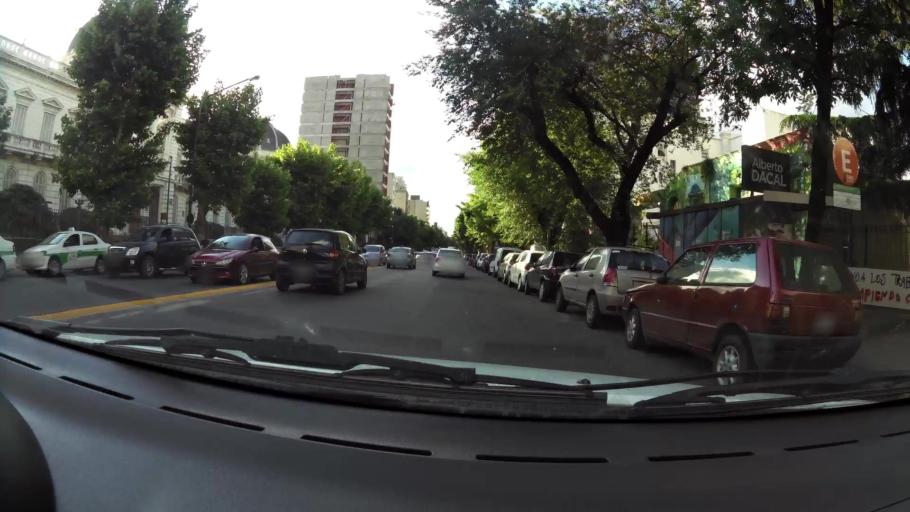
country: AR
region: Buenos Aires
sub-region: Partido de La Plata
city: La Plata
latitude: -34.9193
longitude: -57.9575
